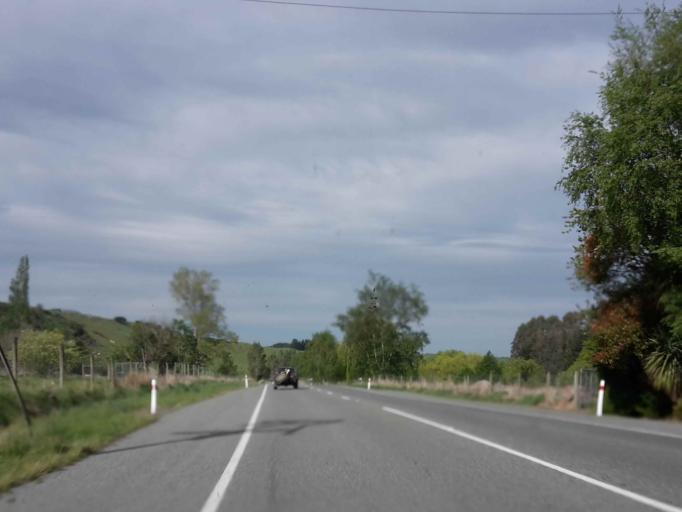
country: NZ
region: Canterbury
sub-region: Timaru District
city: Pleasant Point
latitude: -44.1116
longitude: 171.1467
